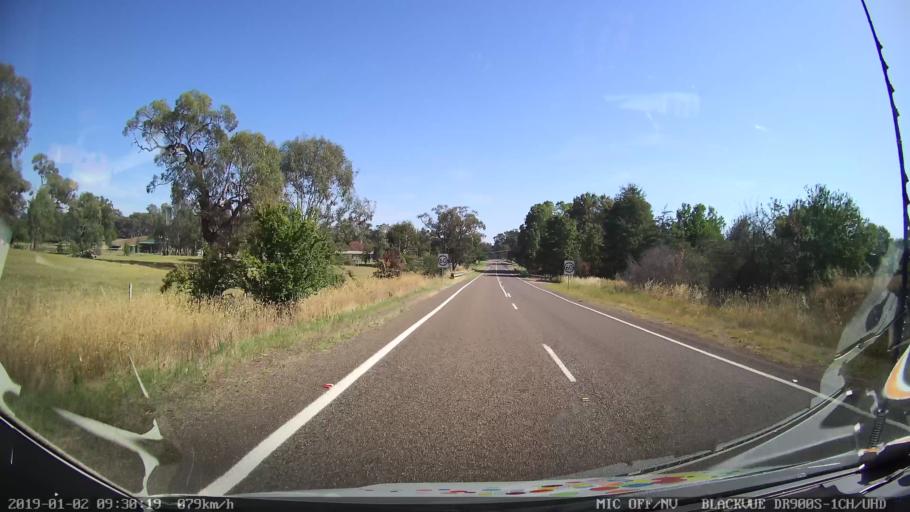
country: AU
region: New South Wales
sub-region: Tumut Shire
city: Tumut
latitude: -35.3279
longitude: 148.2376
